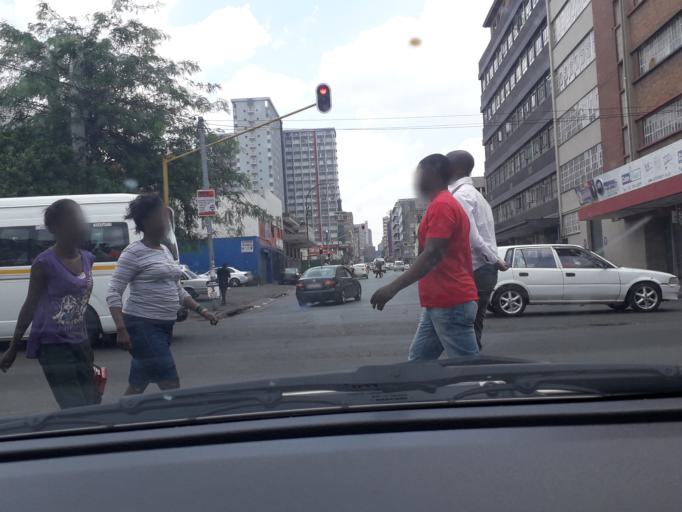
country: ZA
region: Gauteng
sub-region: City of Johannesburg Metropolitan Municipality
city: Johannesburg
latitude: -26.2057
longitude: 28.0529
